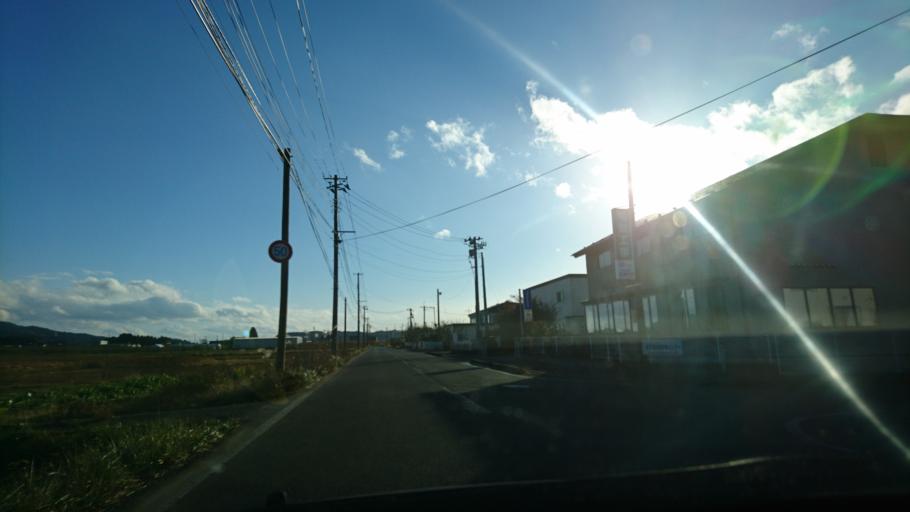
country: JP
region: Iwate
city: Mizusawa
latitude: 39.0498
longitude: 141.1357
